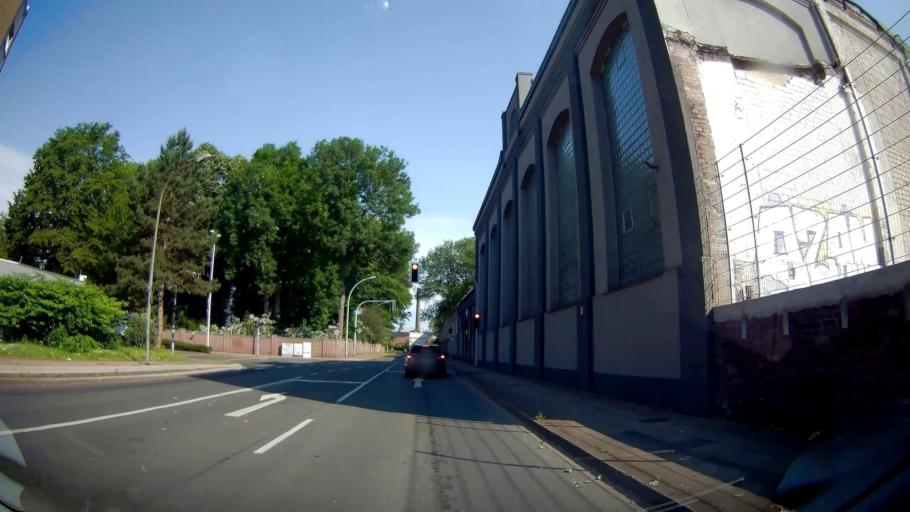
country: DE
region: North Rhine-Westphalia
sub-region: Regierungsbezirk Arnsberg
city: Herne
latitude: 51.5458
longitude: 7.2218
